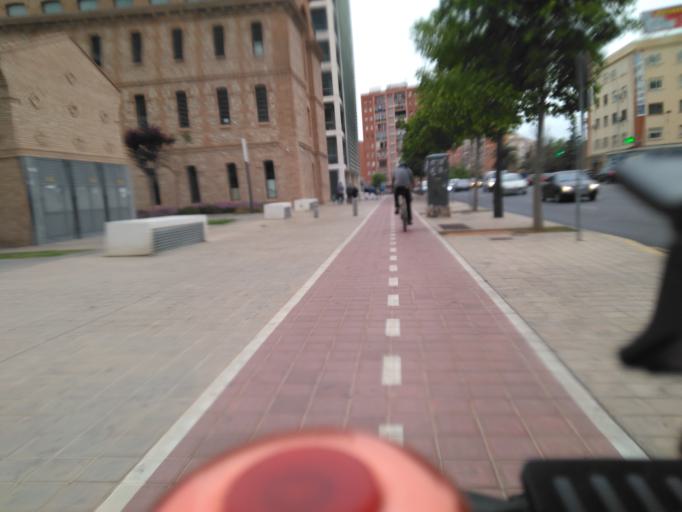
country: ES
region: Valencia
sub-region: Provincia de Valencia
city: Mislata
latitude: 39.4718
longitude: -0.4052
